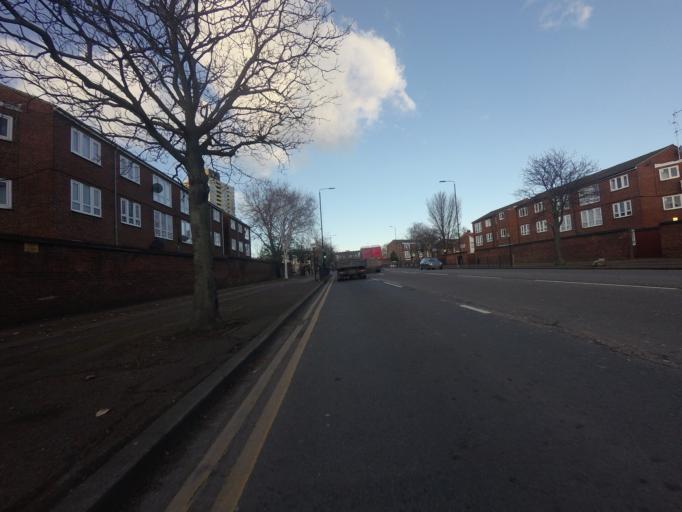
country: GB
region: England
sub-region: Greater London
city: Poplar
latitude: 51.5328
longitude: 0.0078
